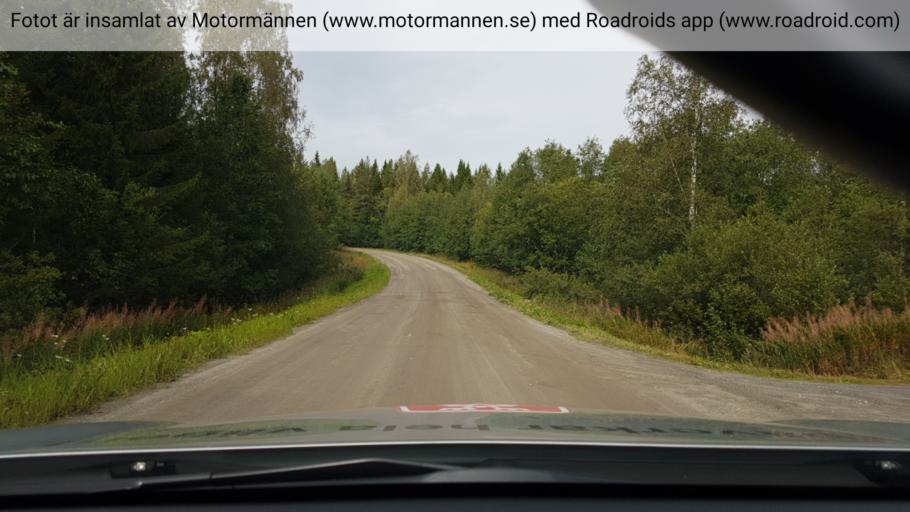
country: SE
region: Vaesterbotten
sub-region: Vannas Kommun
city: Vaennaes
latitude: 63.8418
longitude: 19.6273
